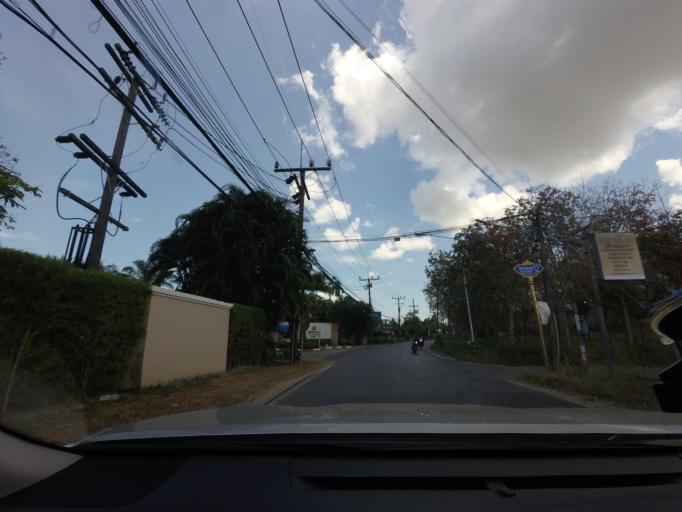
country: TH
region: Phuket
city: Thalang
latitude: 8.0184
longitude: 98.3068
